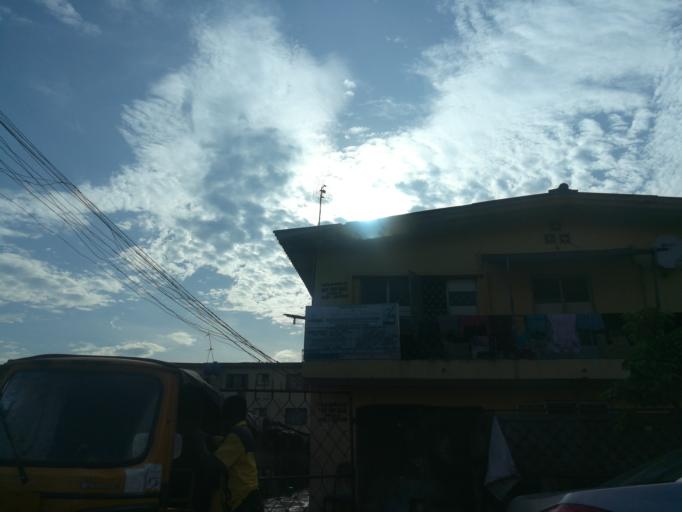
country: NG
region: Lagos
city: Ikeja
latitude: 6.5950
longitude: 3.3451
